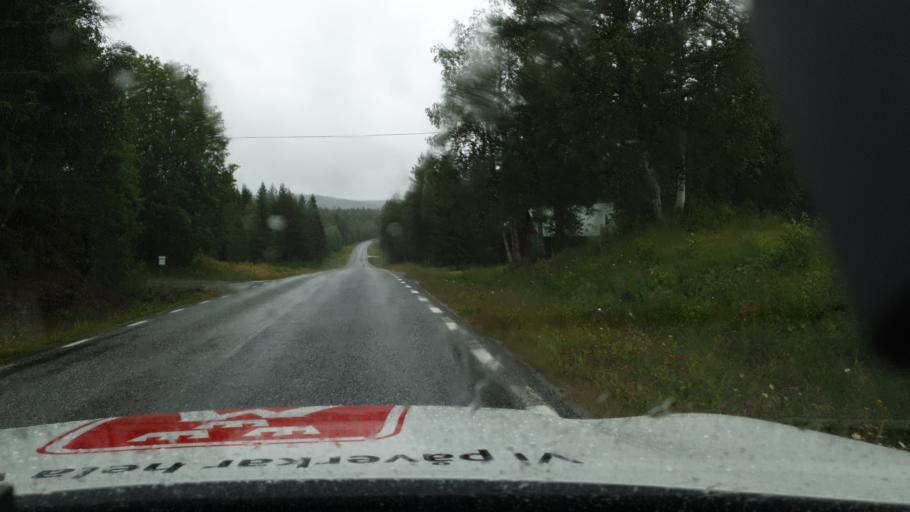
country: SE
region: Vaesterbotten
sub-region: Asele Kommun
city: Insjon
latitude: 64.3314
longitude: 17.7381
